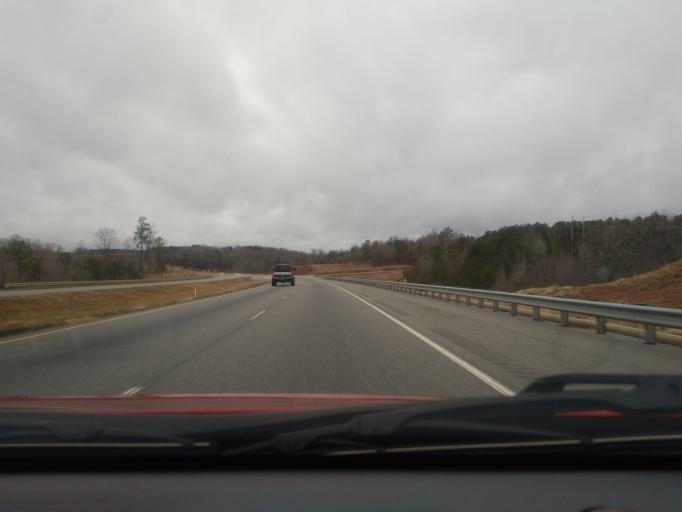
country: US
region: Georgia
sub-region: Henry County
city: Locust Grove
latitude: 33.2605
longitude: -84.1248
